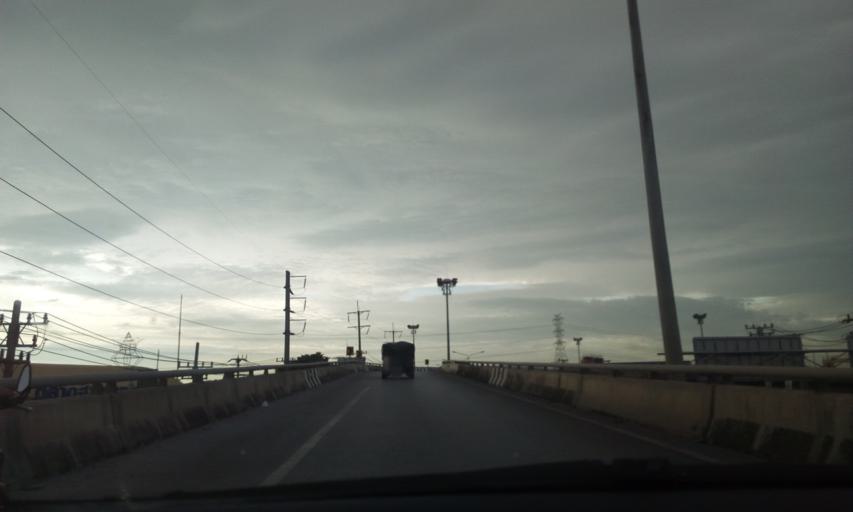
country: TH
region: Phra Nakhon Si Ayutthaya
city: Ban Bang Kadi Pathum Thani
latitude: 13.9717
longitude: 100.5505
